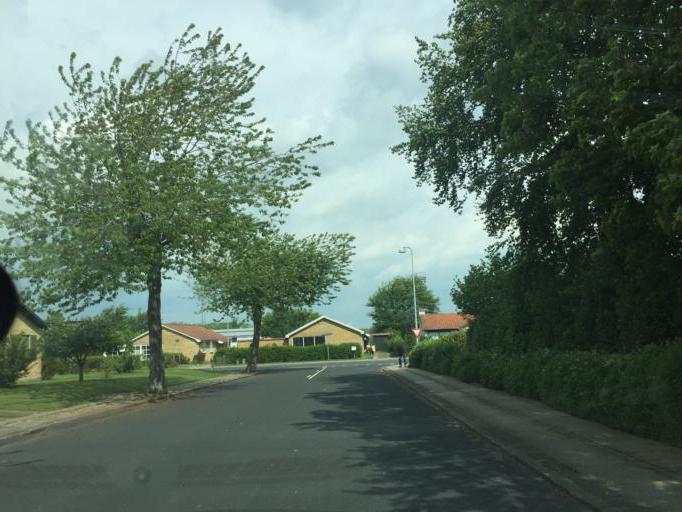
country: DK
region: South Denmark
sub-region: Odense Kommune
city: Odense
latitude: 55.3733
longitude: 10.3524
